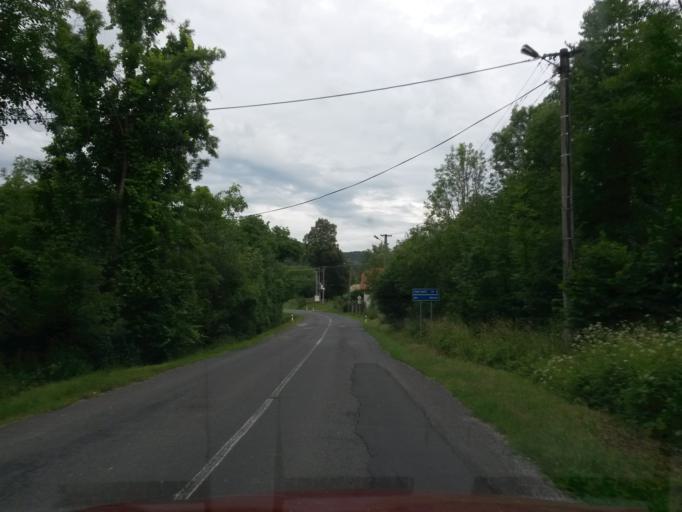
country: SK
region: Banskobystricky
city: Velky Krtis
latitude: 48.3557
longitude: 19.4051
